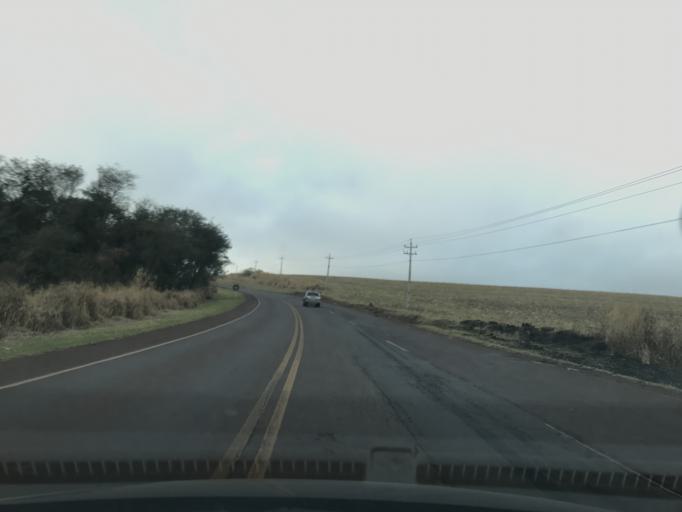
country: BR
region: Parana
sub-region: Toledo
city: Toledo
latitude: -24.6381
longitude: -53.7114
